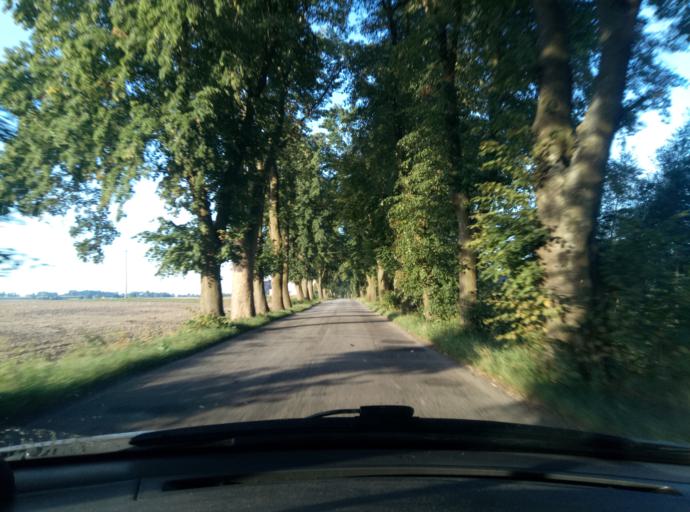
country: PL
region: Kujawsko-Pomorskie
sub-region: Powiat brodnicki
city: Jablonowo Pomorskie
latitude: 53.4064
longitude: 19.1722
